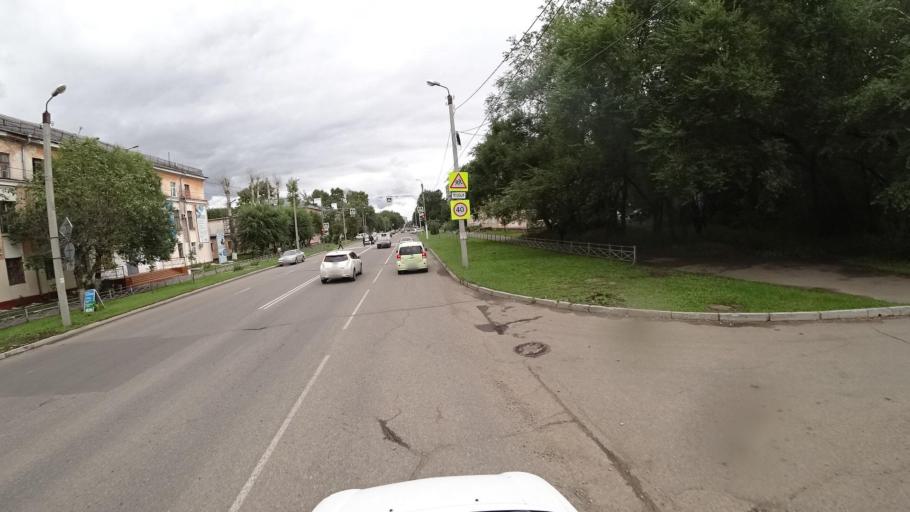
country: RU
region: Khabarovsk Krai
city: Komsomolsk-on-Amur
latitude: 50.5505
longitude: 137.0275
